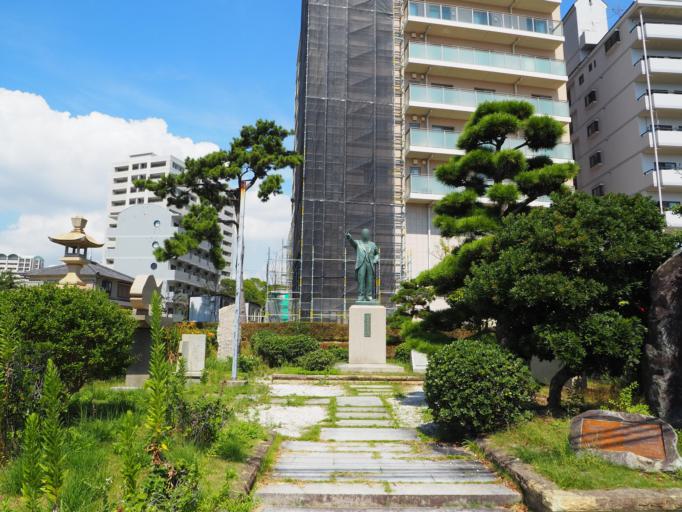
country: JP
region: Hyogo
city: Akashi
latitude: 34.6275
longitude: 135.0545
